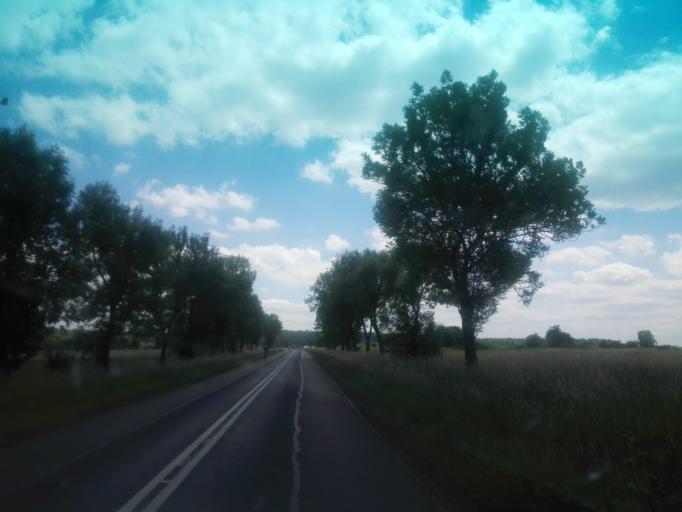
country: PL
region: Silesian Voivodeship
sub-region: Powiat czestochowski
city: Olsztyn
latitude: 50.7505
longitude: 19.3125
